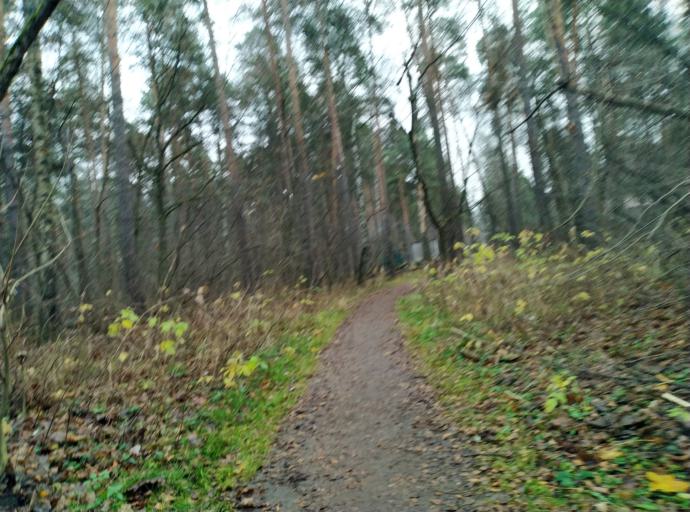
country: RU
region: Moskovskaya
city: Korenevo
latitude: 55.6600
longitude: 38.0012
